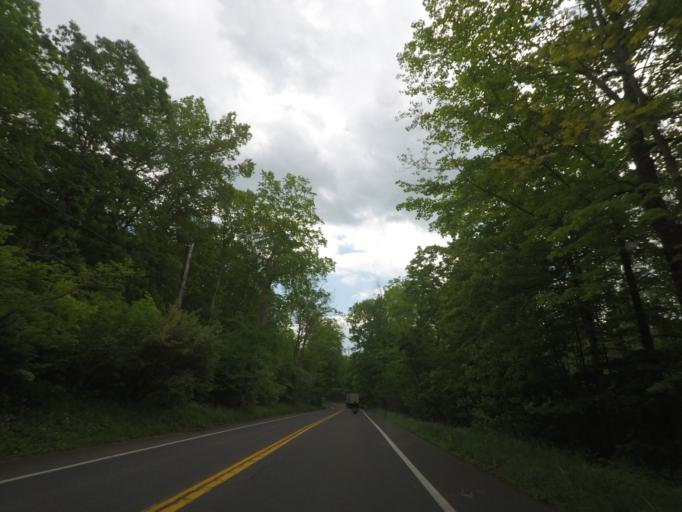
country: US
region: New York
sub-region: Dutchess County
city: Pine Plains
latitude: 42.0684
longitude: -73.6671
